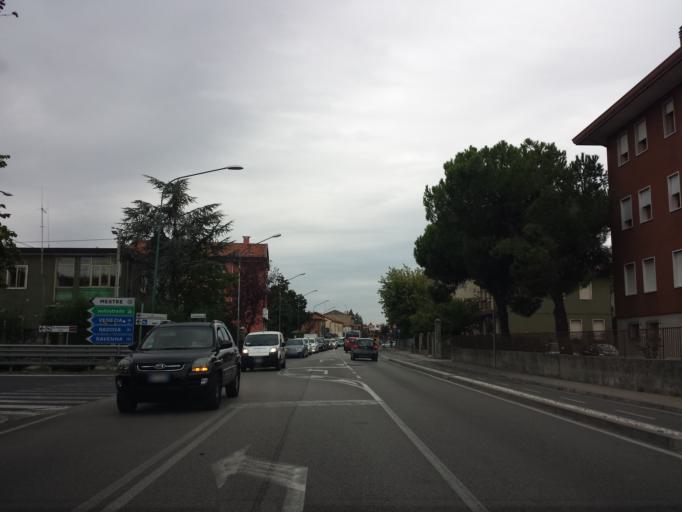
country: IT
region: Veneto
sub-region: Provincia di Venezia
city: Mestre
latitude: 45.4767
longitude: 12.2138
